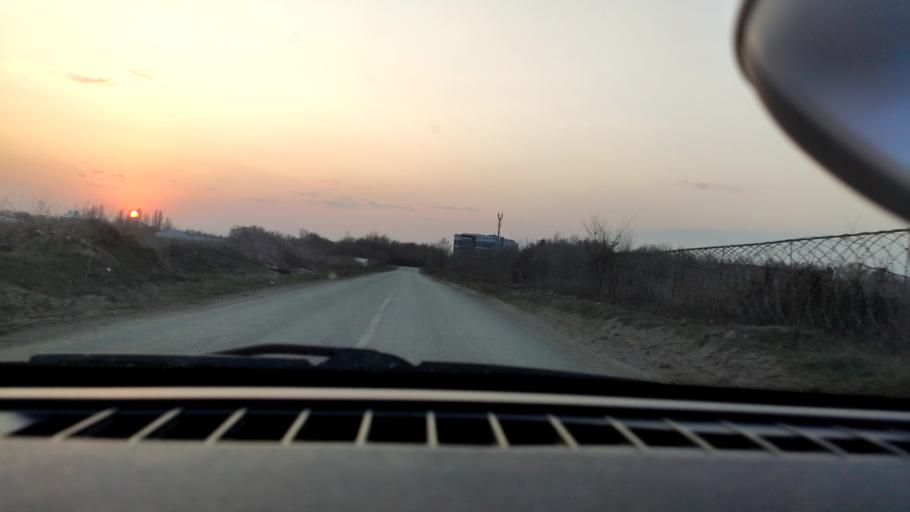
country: RU
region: Samara
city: Smyshlyayevka
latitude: 53.2062
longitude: 50.3140
